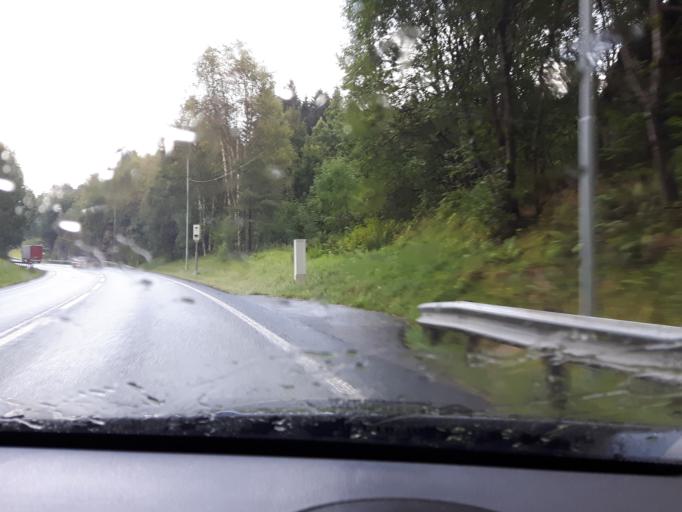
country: NO
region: Vest-Agder
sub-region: Sogne
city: Sogne
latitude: 58.0933
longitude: 7.7661
